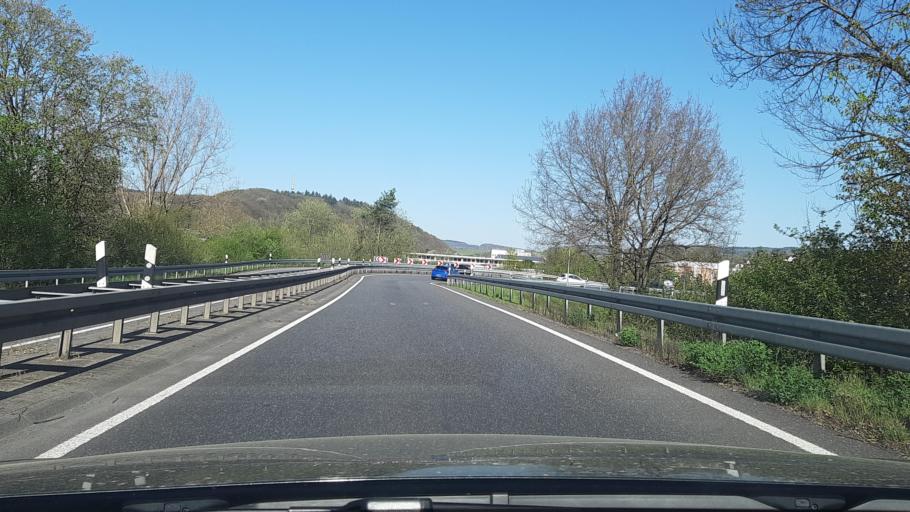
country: DE
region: Hesse
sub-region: Regierungsbezirk Giessen
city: Asslar
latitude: 50.5812
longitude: 8.4749
